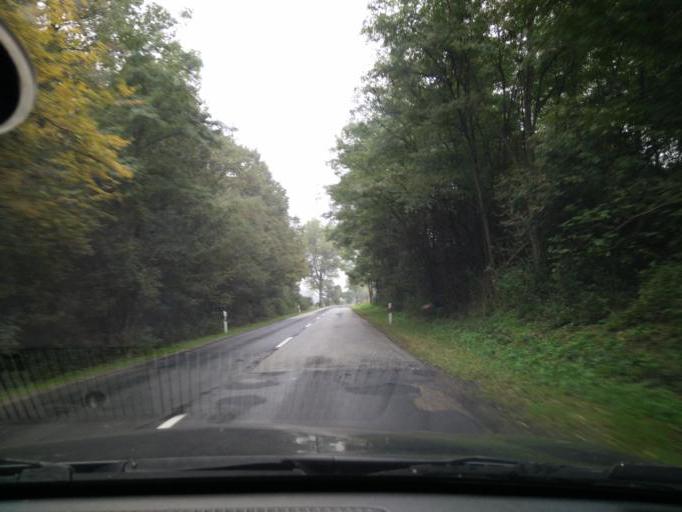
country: HU
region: Komarom-Esztergom
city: Tarjan
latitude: 47.5792
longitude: 18.4815
